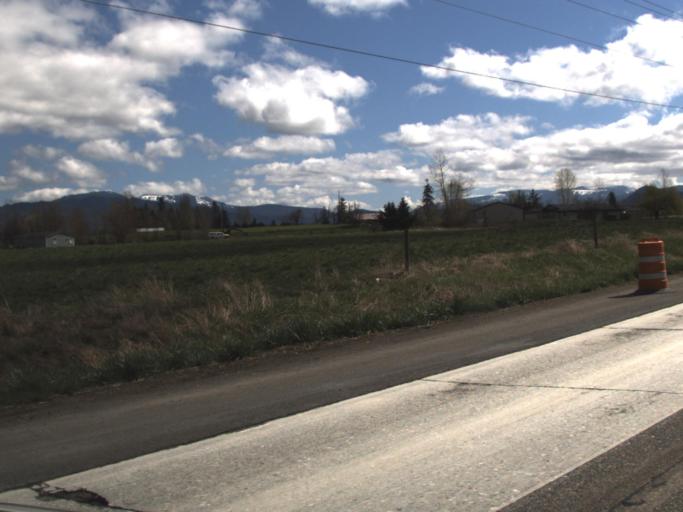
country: US
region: Washington
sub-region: Pierce County
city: Buckley
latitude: 47.2132
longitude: -122.0838
